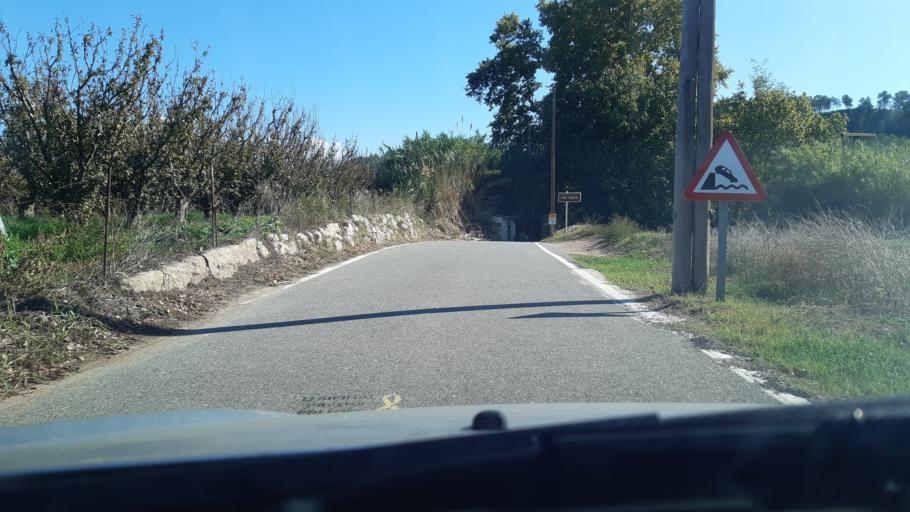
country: ES
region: Catalonia
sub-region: Provincia de Tarragona
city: Miravet
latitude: 41.0335
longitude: 0.6078
